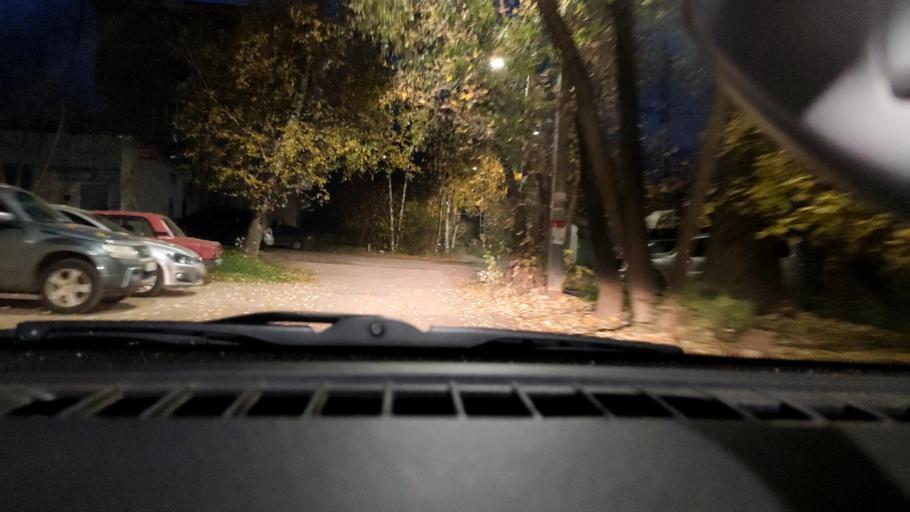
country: RU
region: Perm
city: Perm
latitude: 57.9936
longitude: 56.2327
